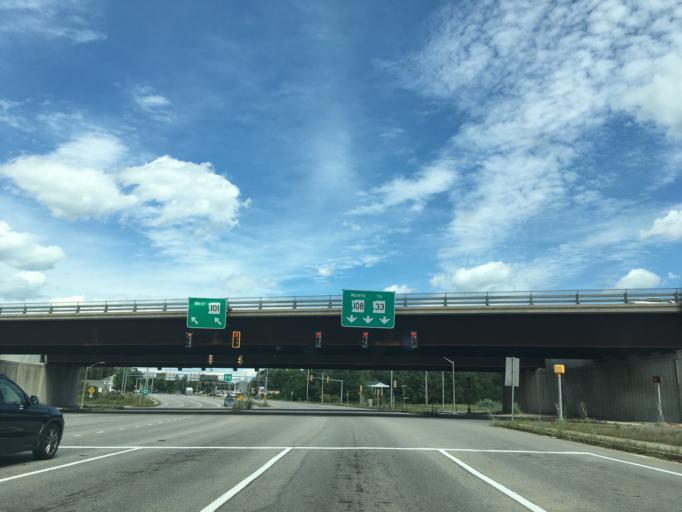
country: US
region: New Hampshire
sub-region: Rockingham County
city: Exeter
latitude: 42.9919
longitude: -70.9271
